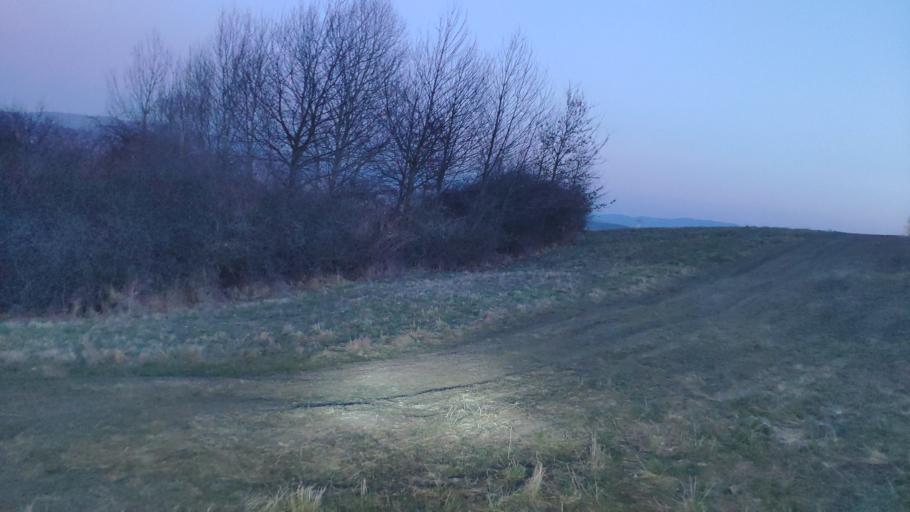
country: SK
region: Kosicky
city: Kosice
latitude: 48.8334
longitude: 21.2568
